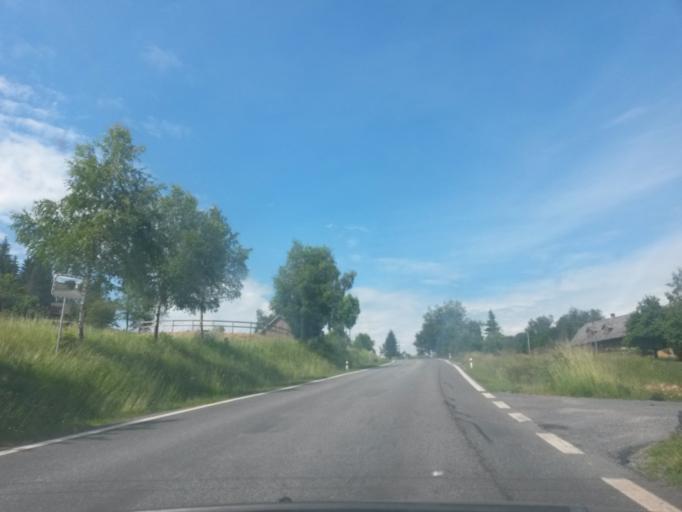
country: CZ
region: Vysocina
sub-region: Okres Zd'ar nad Sazavou
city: Jimramov
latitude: 49.6035
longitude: 16.1550
